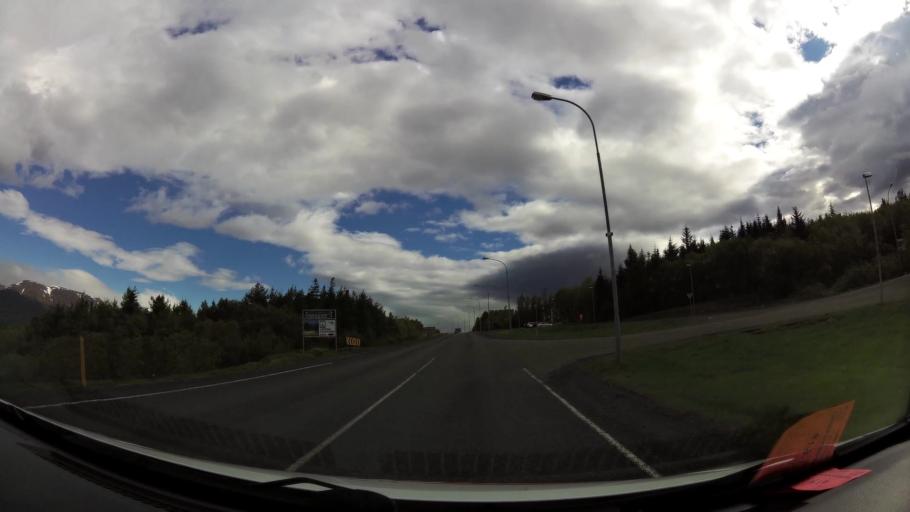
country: IS
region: Northwest
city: Saudarkrokur
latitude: 65.5527
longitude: -19.4447
